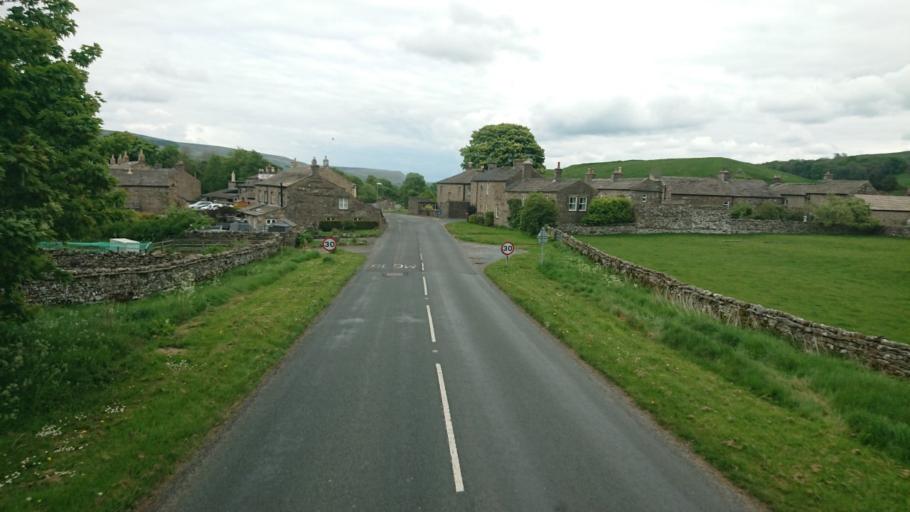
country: GB
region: England
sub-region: County Durham
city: Bowes
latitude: 54.3084
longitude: -2.1051
